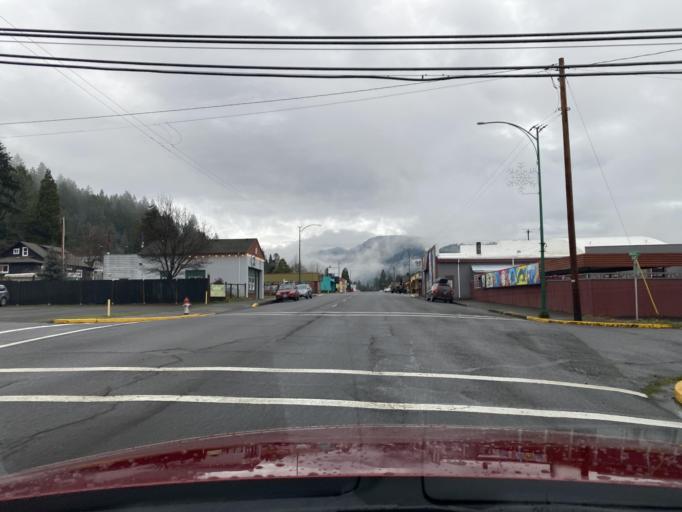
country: US
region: Oregon
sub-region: Lane County
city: Oakridge
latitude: 43.7479
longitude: -122.4614
